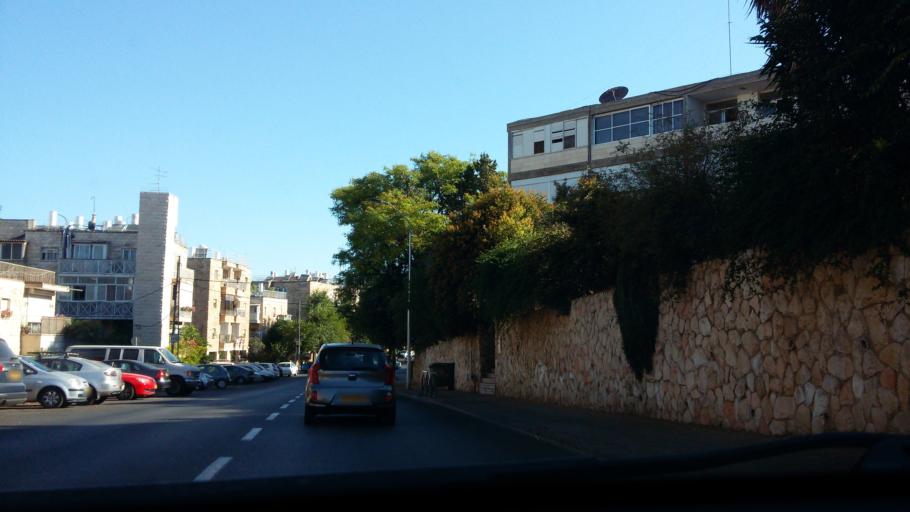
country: IL
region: Jerusalem
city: Jerusalem
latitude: 31.7661
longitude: 35.2060
